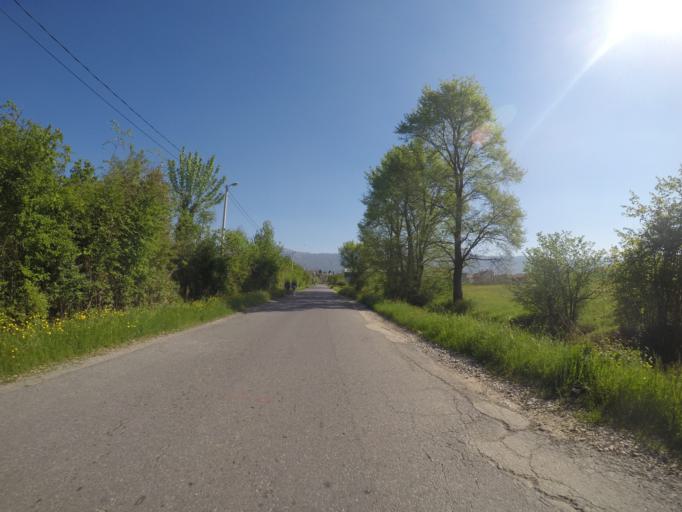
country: ME
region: Danilovgrad
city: Danilovgrad
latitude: 42.5433
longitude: 19.0966
